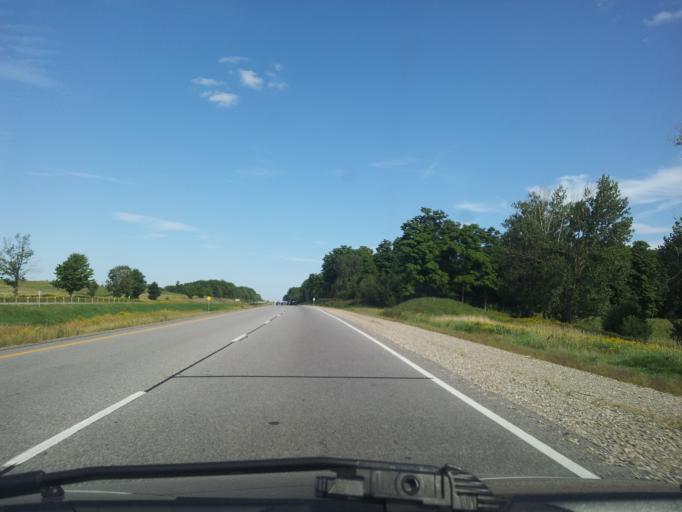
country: CA
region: Ontario
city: Kitchener
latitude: 43.3969
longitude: -80.6334
